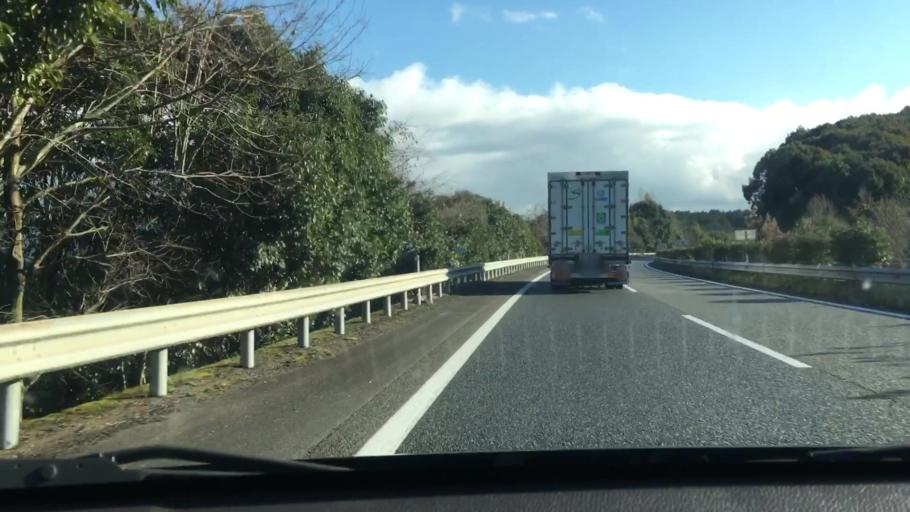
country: JP
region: Kumamoto
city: Hitoyoshi
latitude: 32.1701
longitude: 130.7920
